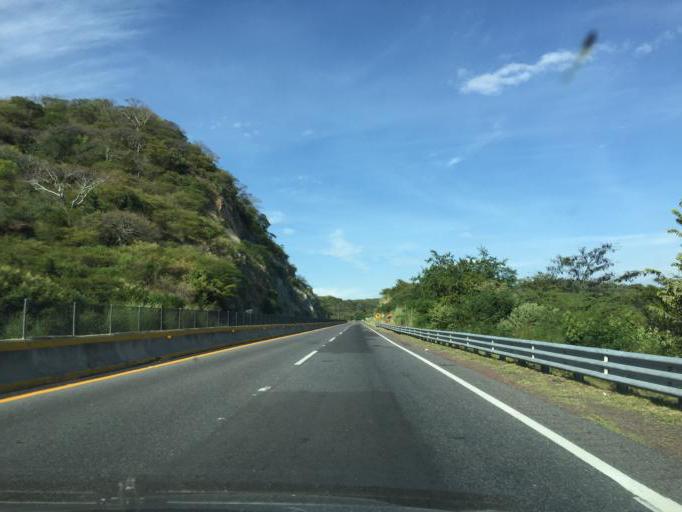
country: MX
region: Morelos
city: Tilzapotla
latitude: 18.3757
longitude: -99.1782
